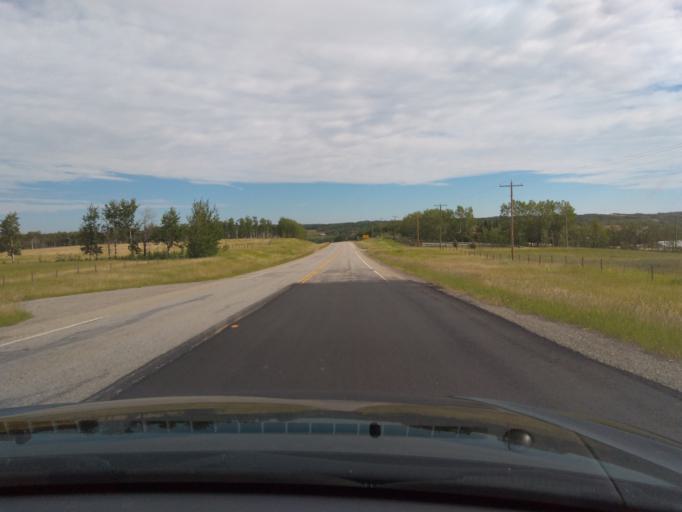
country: CA
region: Alberta
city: Cochrane
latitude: 51.3648
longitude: -114.4725
